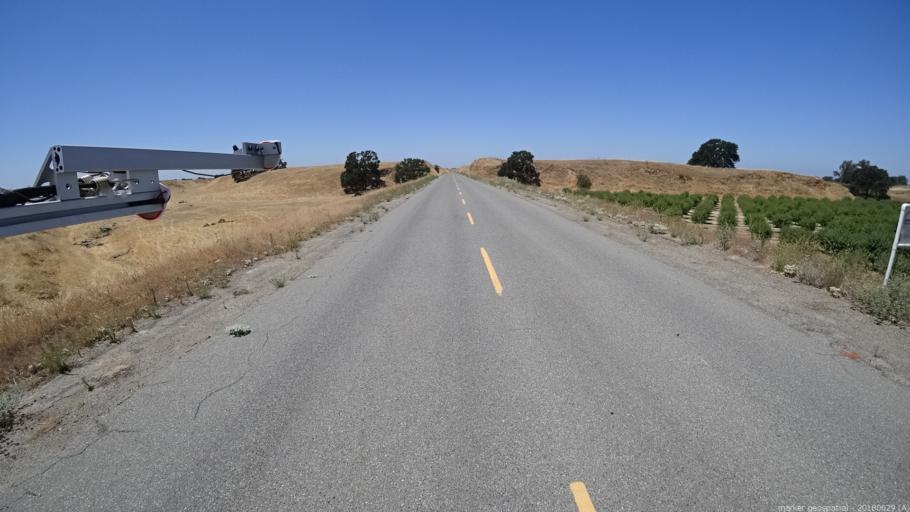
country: US
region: California
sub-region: Madera County
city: Bonadelle Ranchos-Madera Ranchos
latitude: 37.0451
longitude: -119.9229
